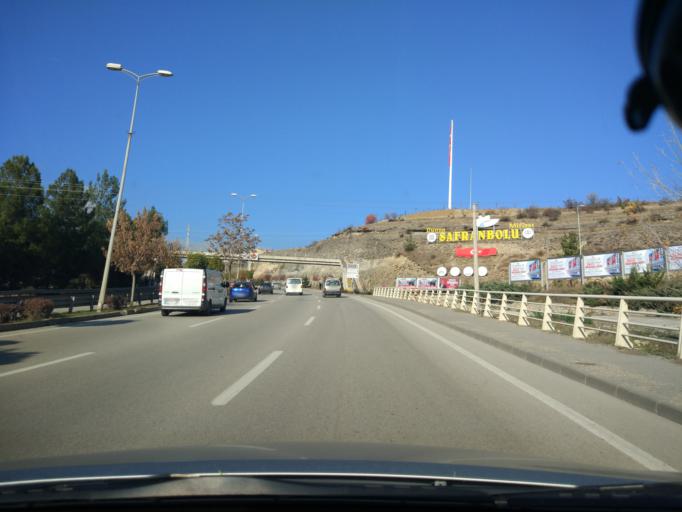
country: TR
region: Karabuk
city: Safranbolu
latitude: 41.2319
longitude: 32.6723
